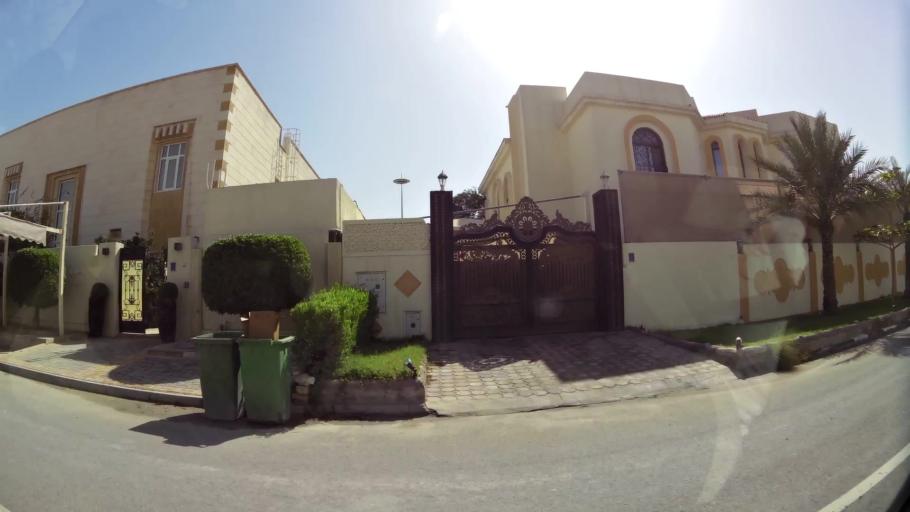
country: QA
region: Baladiyat ad Dawhah
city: Doha
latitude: 25.3584
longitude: 51.5192
